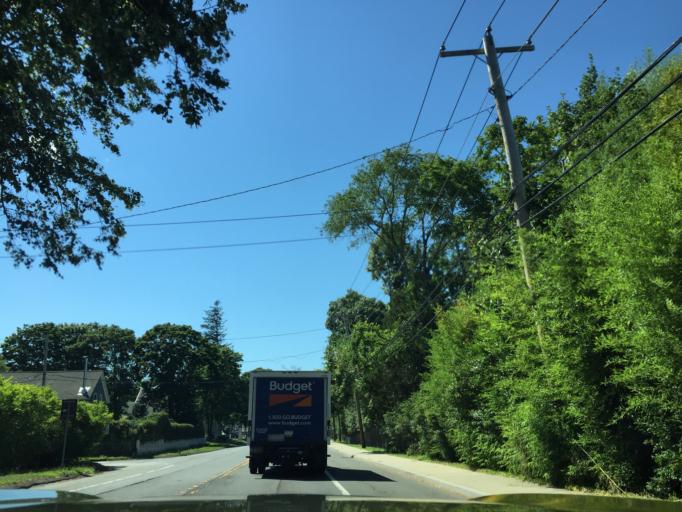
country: US
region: New York
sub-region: Suffolk County
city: Sag Harbor
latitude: 40.9964
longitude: -72.2852
